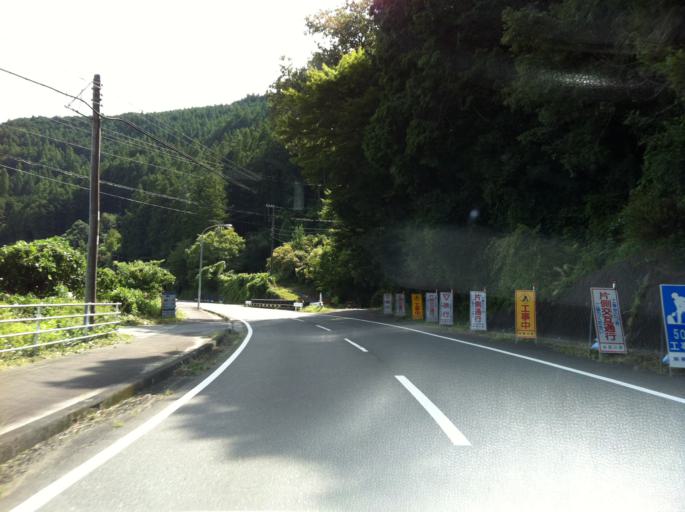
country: JP
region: Shizuoka
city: Kanaya
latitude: 35.0586
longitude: 138.0877
